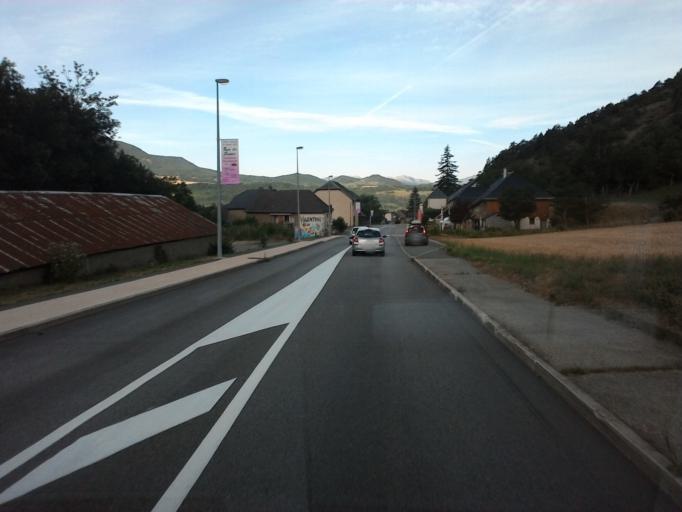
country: FR
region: Rhone-Alpes
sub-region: Departement de l'Isere
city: La Mure
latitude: 44.8645
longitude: 5.8628
